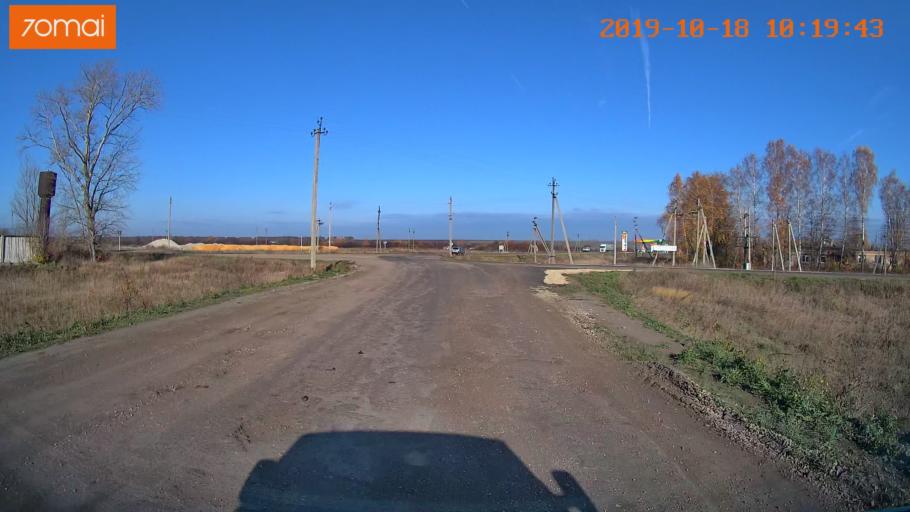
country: RU
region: Tula
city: Kurkino
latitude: 53.4240
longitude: 38.6451
